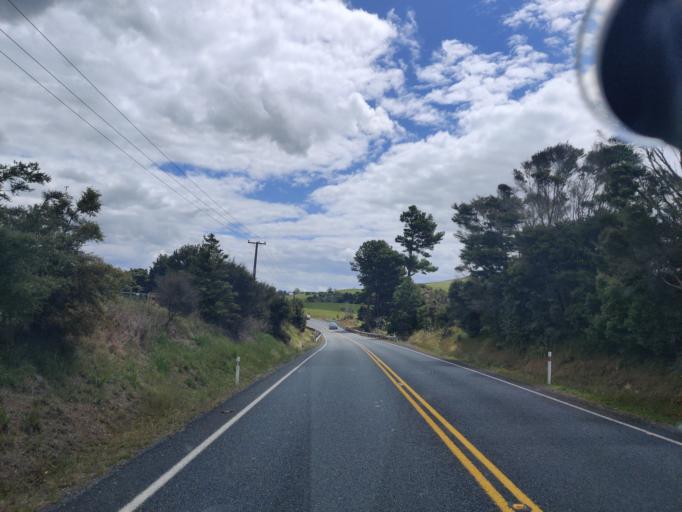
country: NZ
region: Northland
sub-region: Far North District
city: Paihia
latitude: -35.2813
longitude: 174.0401
